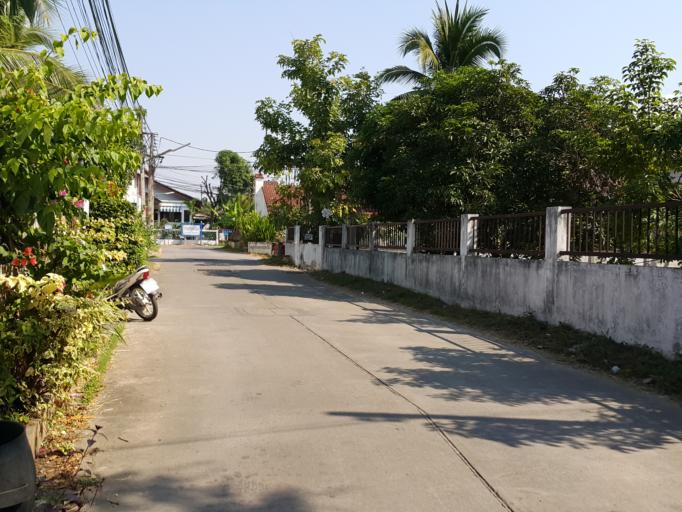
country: TH
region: Lampang
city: Lampang
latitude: 18.3005
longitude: 99.4942
